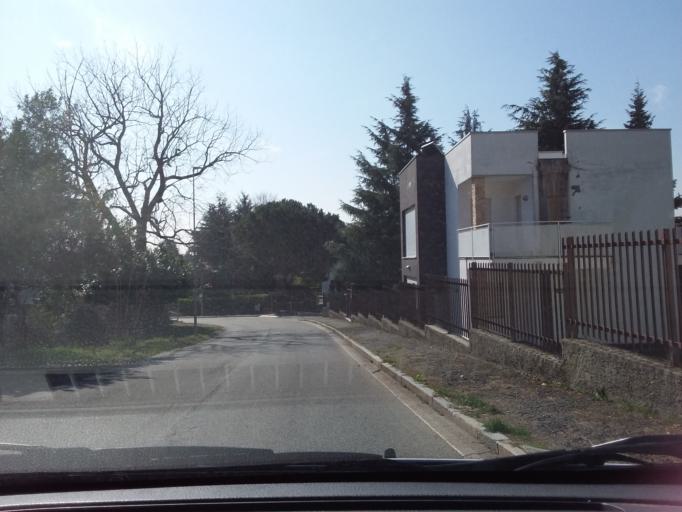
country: IT
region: Piedmont
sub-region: Provincia di Torino
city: Rivoli
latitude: 45.0805
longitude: 7.5244
